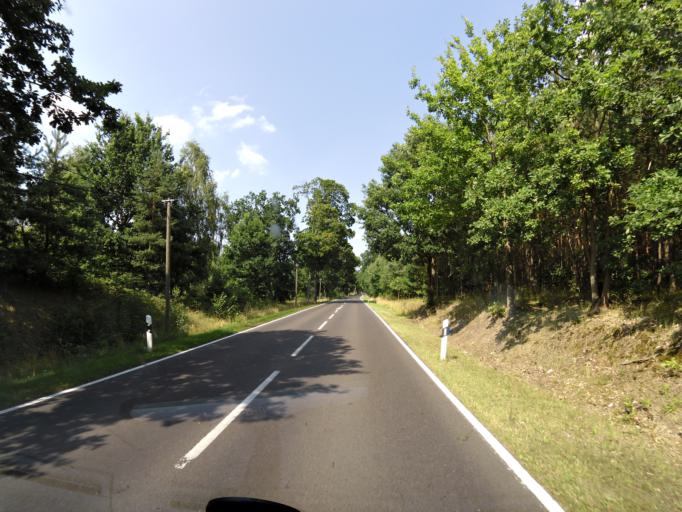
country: DE
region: Brandenburg
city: Liebenwalde
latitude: 52.8843
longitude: 13.3965
